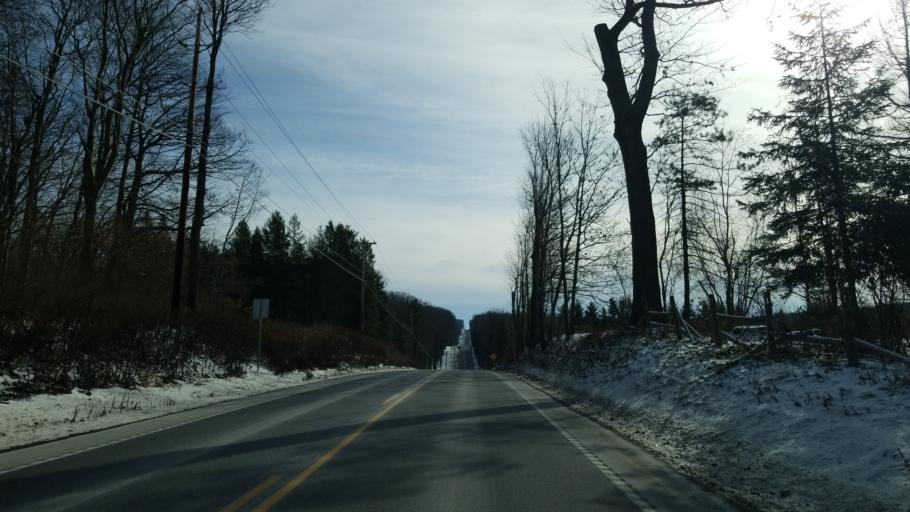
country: US
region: Pennsylvania
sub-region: Clearfield County
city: Clearfield
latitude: 41.1480
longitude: -78.5462
